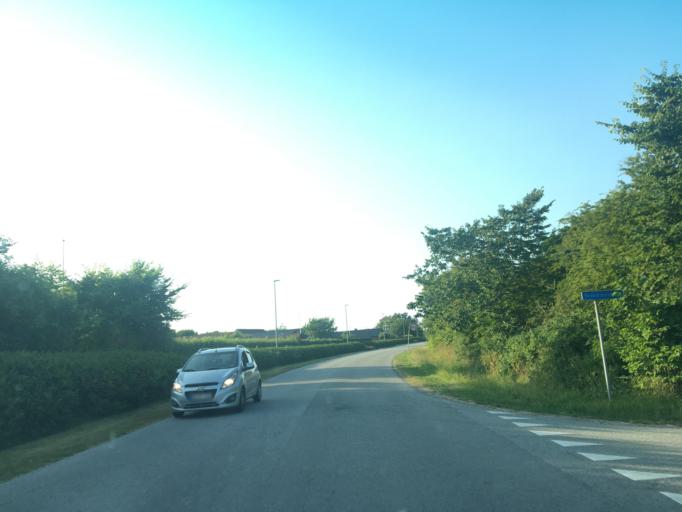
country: DK
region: North Denmark
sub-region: Thisted Kommune
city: Hurup
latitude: 56.7549
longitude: 8.4242
